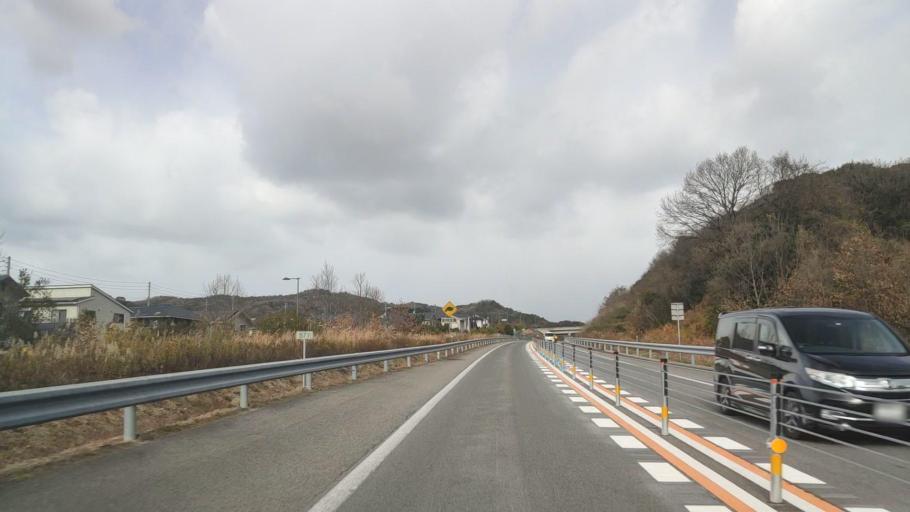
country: JP
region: Ehime
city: Hojo
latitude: 34.0668
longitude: 132.9735
